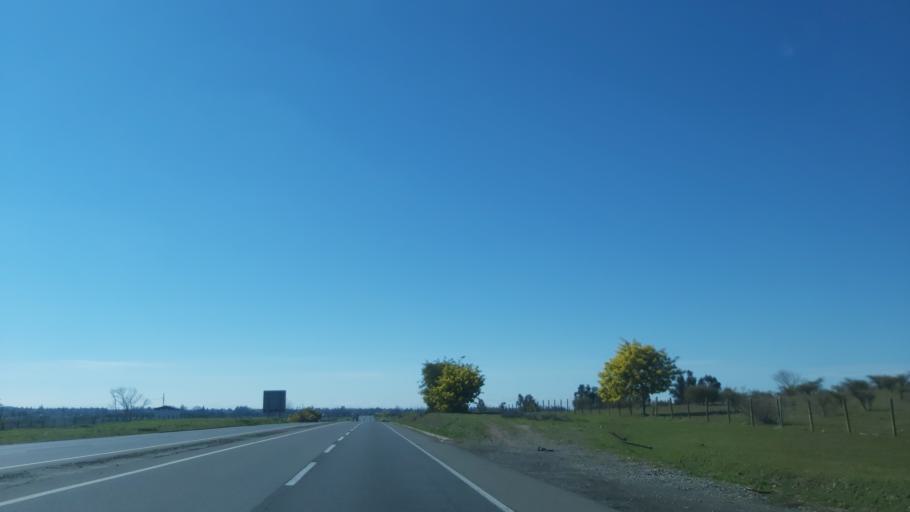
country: CL
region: Biobio
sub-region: Provincia de Nuble
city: Bulnes
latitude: -36.6593
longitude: -72.2536
